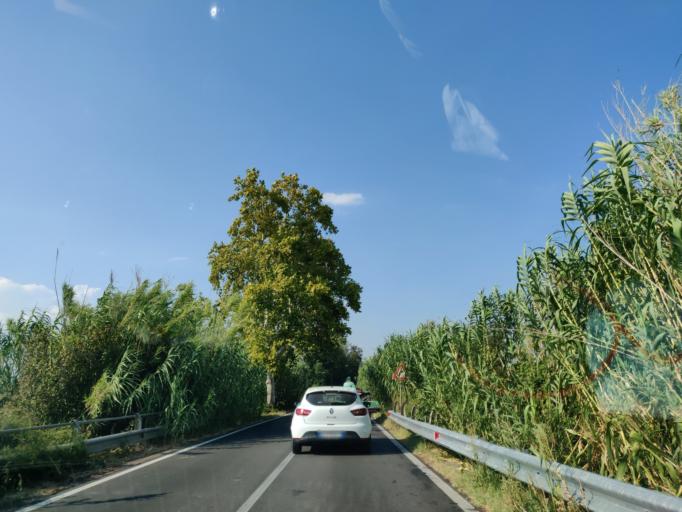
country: IT
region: Latium
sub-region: Provincia di Viterbo
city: Canino
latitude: 42.4063
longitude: 11.6953
